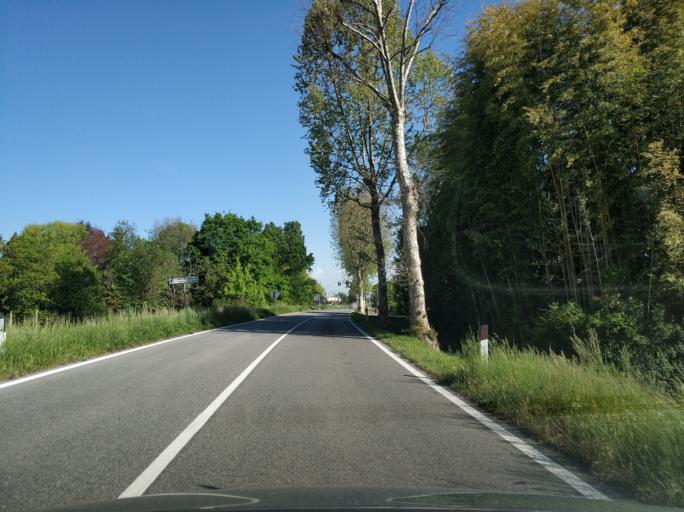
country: IT
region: Friuli Venezia Giulia
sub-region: Provincia di Udine
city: Terzo d'Aquileia
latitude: 45.8054
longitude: 13.3442
